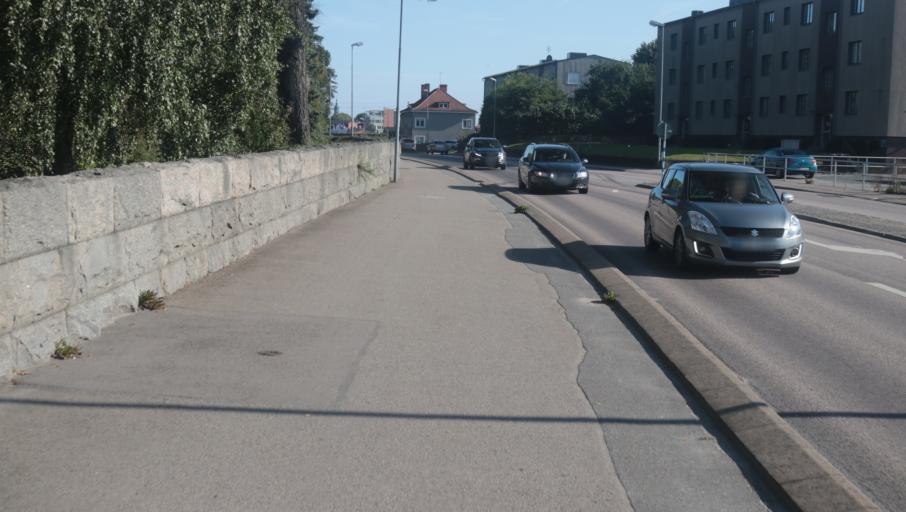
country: SE
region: Blekinge
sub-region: Karlshamns Kommun
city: Karlshamn
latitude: 56.1806
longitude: 14.8529
